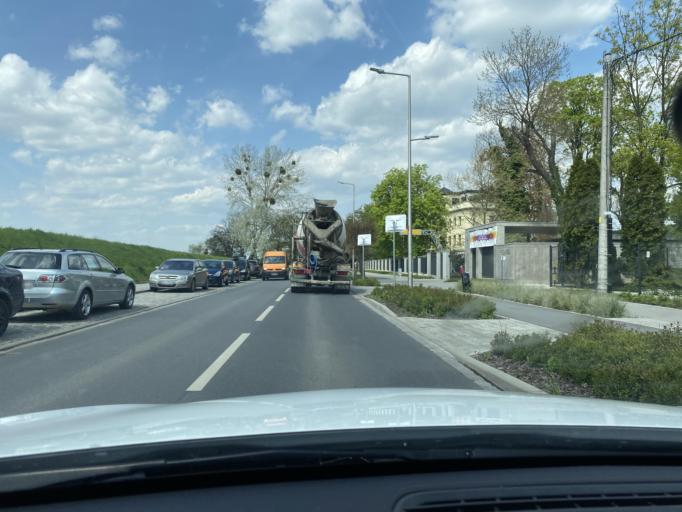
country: PL
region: Lower Silesian Voivodeship
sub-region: Powiat wroclawski
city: Wroclaw
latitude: 51.1383
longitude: 16.9923
